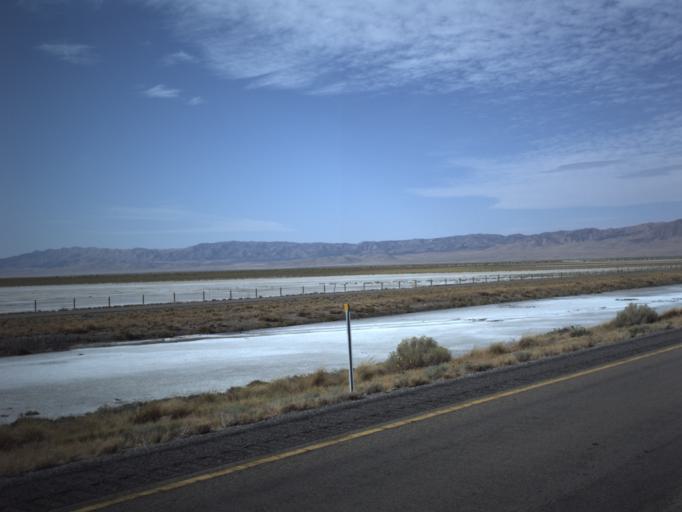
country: US
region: Utah
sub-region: Tooele County
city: Grantsville
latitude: 40.7513
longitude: -112.7049
